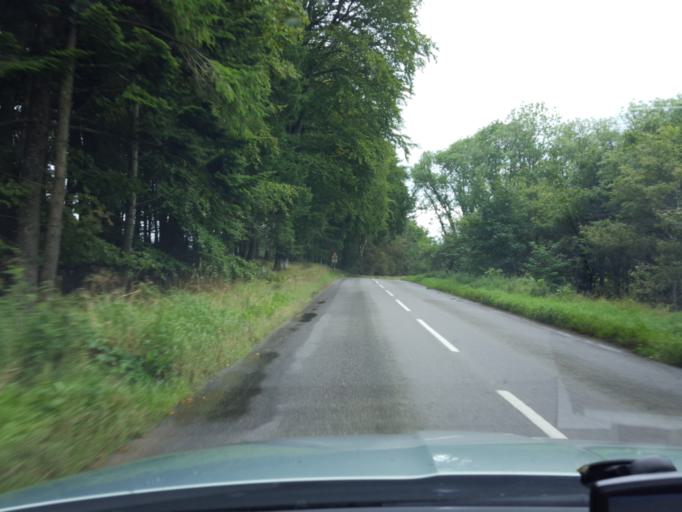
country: GB
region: Scotland
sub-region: Aberdeenshire
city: Kemnay
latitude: 57.1567
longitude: -2.4305
